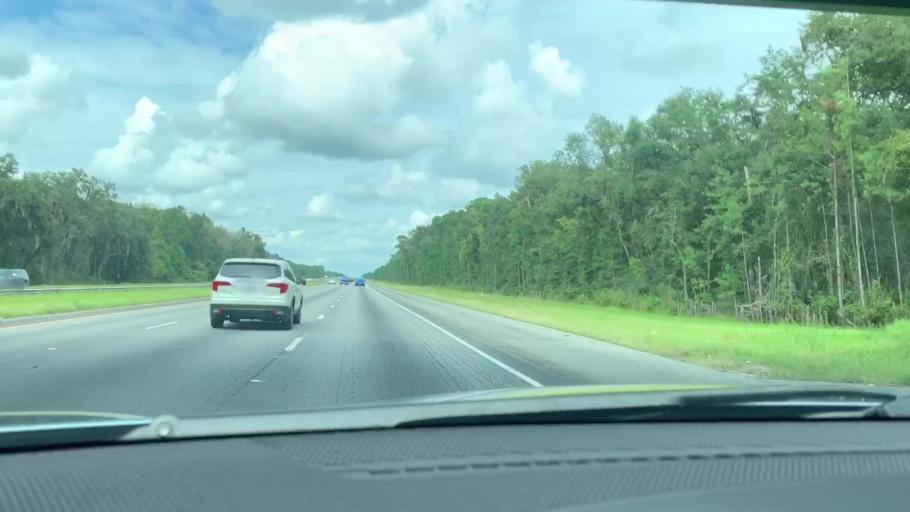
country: US
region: Georgia
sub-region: Liberty County
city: Midway
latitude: 31.5995
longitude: -81.4218
